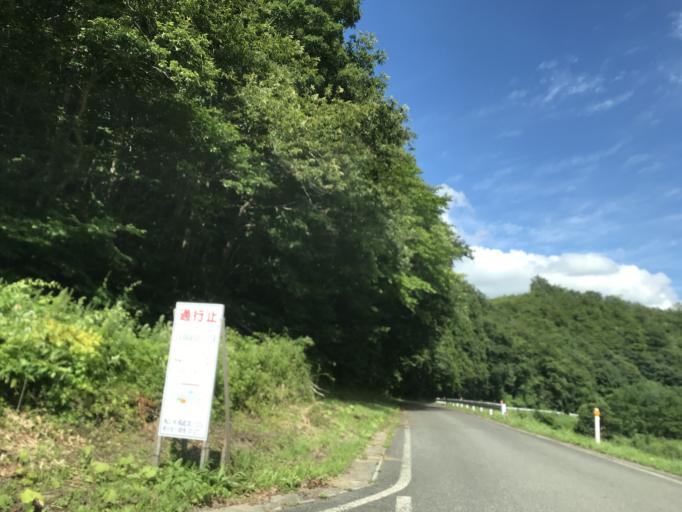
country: JP
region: Iwate
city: Ichinoseki
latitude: 38.9612
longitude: 140.9721
